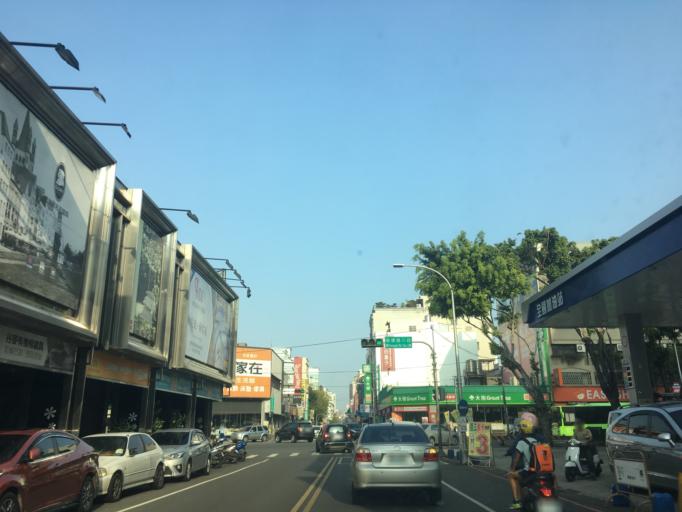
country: TW
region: Taiwan
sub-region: Taichung City
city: Taichung
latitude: 24.1695
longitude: 120.6858
